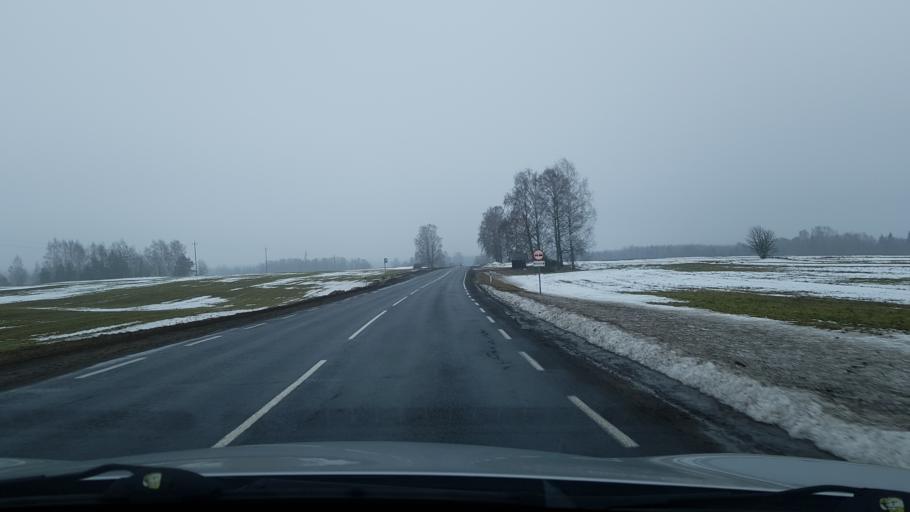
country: EE
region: Viljandimaa
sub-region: Viiratsi vald
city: Viiratsi
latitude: 58.2586
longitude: 25.7158
